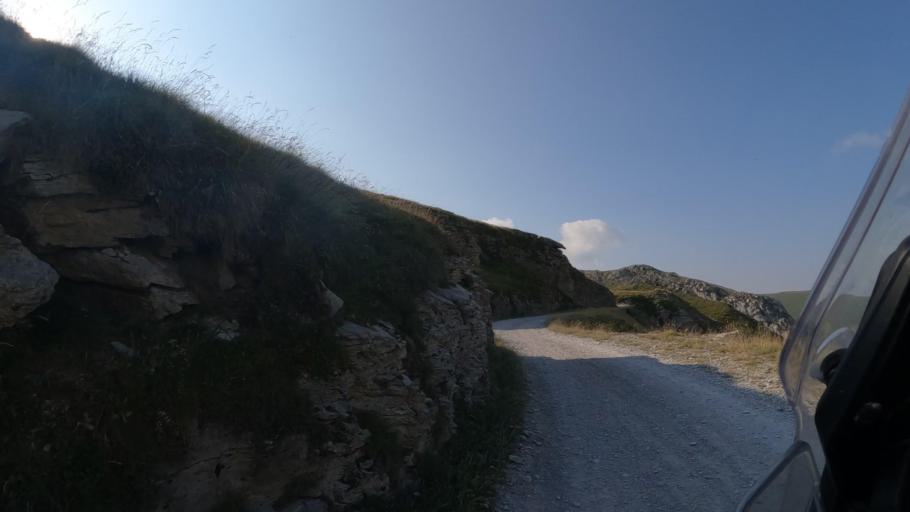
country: IT
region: Piedmont
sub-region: Provincia di Cuneo
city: Limone Piemonte
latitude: 44.1714
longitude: 7.6391
